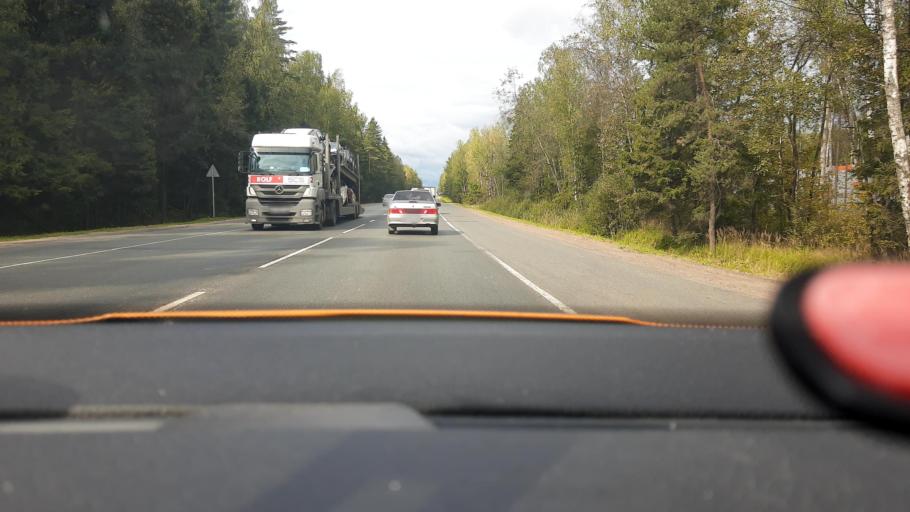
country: RU
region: Moskovskaya
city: Zelenogradskiy
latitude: 56.0897
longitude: 37.9901
